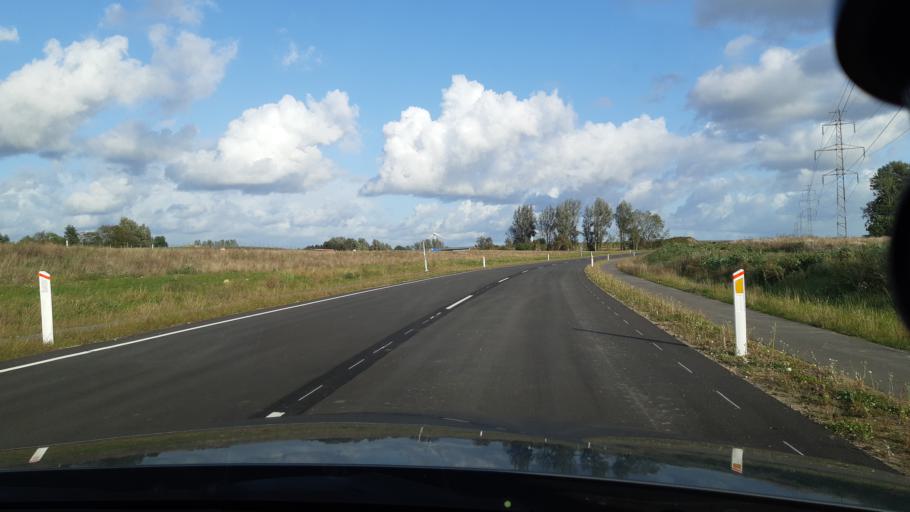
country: DK
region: Zealand
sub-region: Holbaek Kommune
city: Holbaek
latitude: 55.6605
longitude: 11.6092
